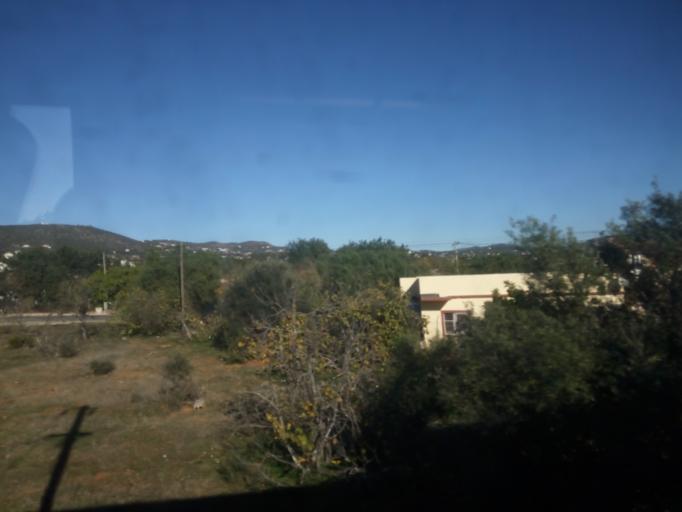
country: PT
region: Faro
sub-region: Faro
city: Santa Barbara de Nexe
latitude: 37.0872
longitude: -7.9917
